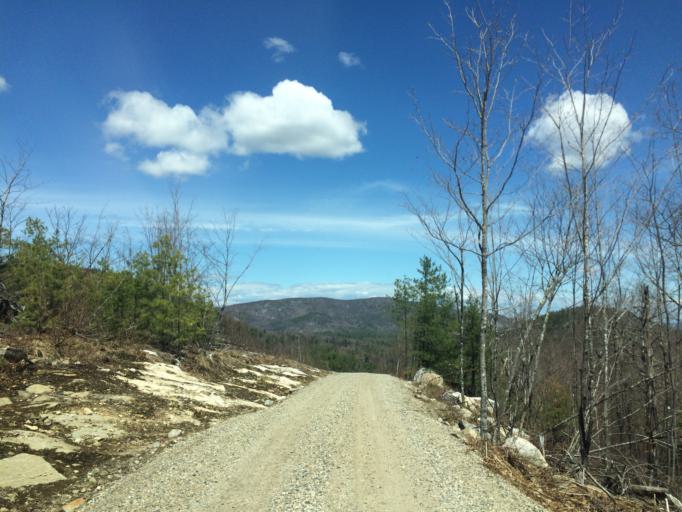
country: US
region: Maine
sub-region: Oxford County
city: Porter
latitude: 43.8498
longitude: -70.9150
